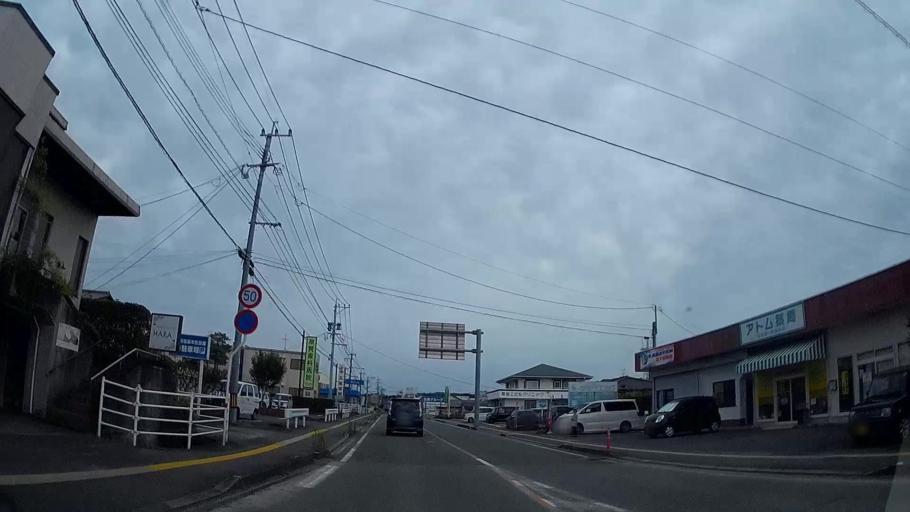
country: JP
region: Kumamoto
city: Kikuchi
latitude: 32.9752
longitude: 130.8081
